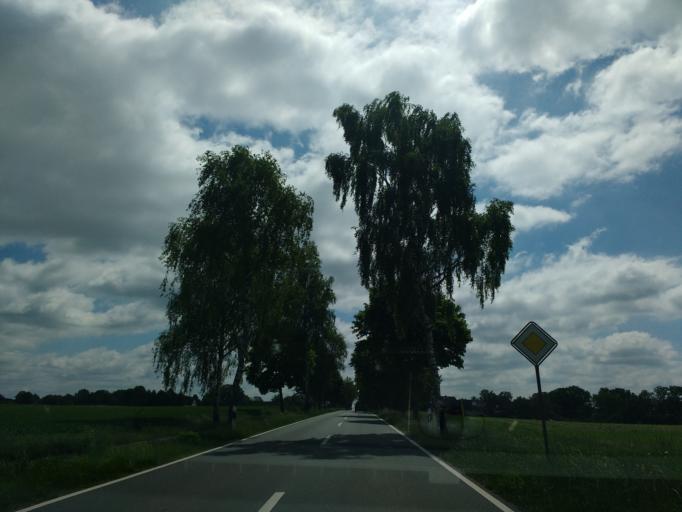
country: DE
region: Lower Saxony
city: Walsrode
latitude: 52.8370
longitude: 9.6273
